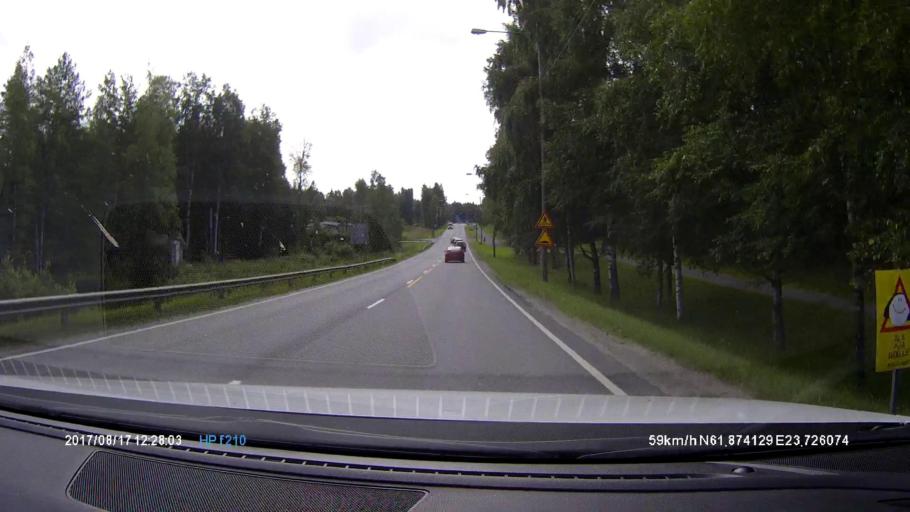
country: FI
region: Pirkanmaa
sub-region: Tampere
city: Kuru
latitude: 61.8738
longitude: 23.7262
